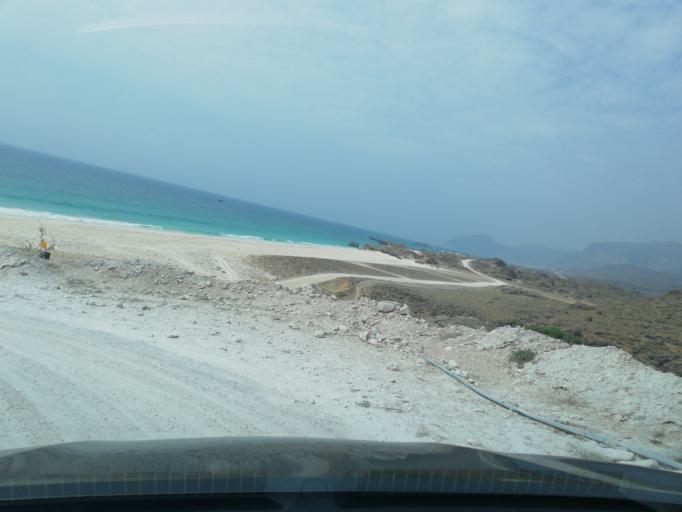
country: OM
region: Zufar
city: Salalah
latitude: 16.8414
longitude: 53.7214
